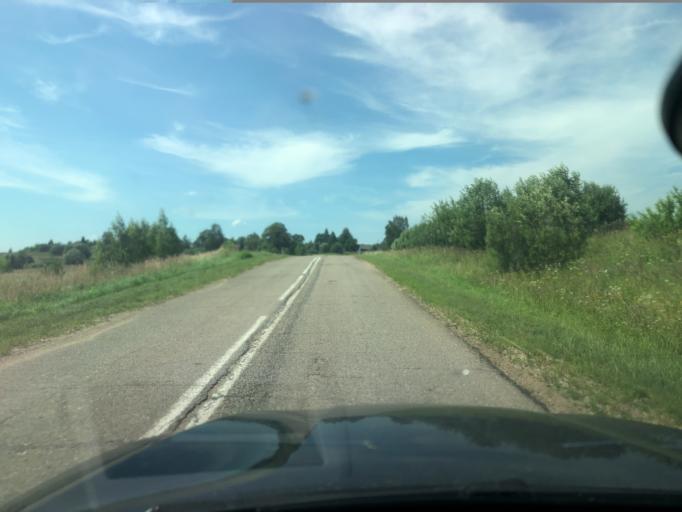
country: RU
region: Jaroslavl
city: Pereslavl'-Zalesskiy
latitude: 57.0375
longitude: 38.9000
